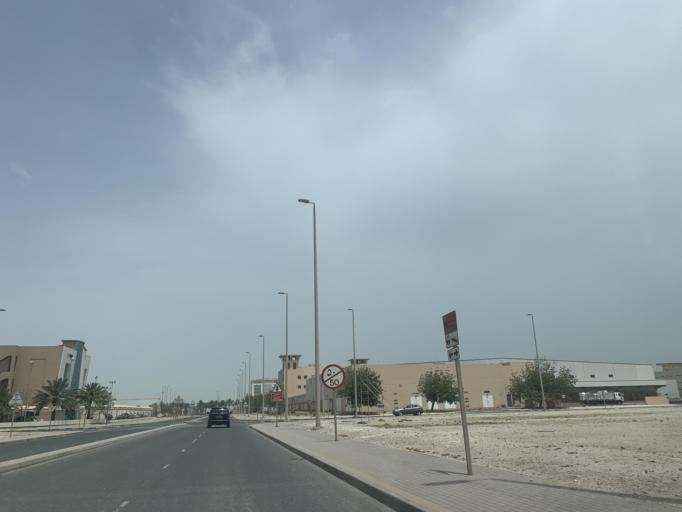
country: BH
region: Muharraq
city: Al Hadd
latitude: 26.2174
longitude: 50.6742
